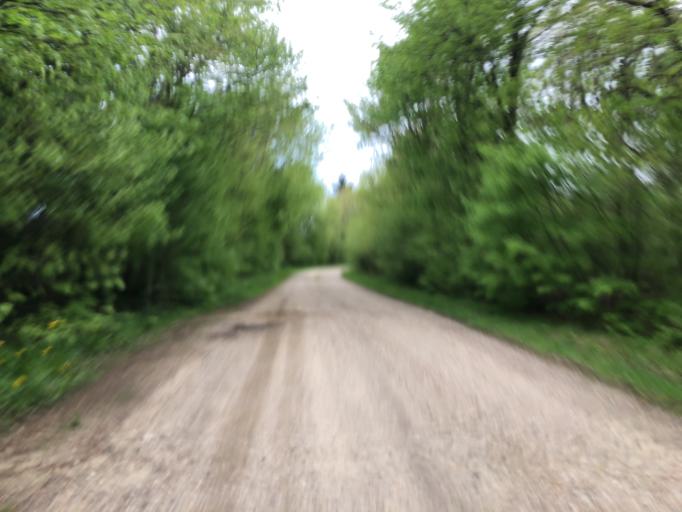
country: DK
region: Central Jutland
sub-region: Holstebro Kommune
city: Ulfborg
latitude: 56.2671
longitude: 8.4258
